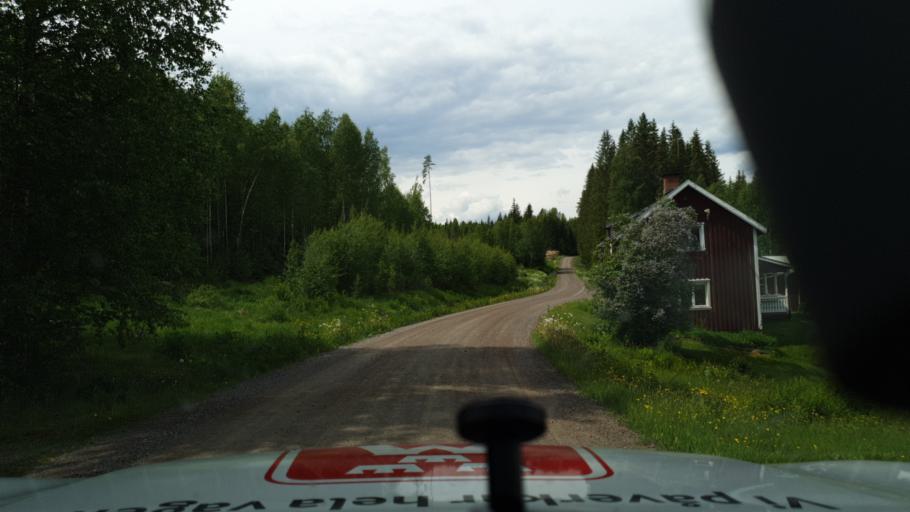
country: SE
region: Vaermland
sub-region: Torsby Kommun
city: Torsby
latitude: 59.9781
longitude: 12.8465
